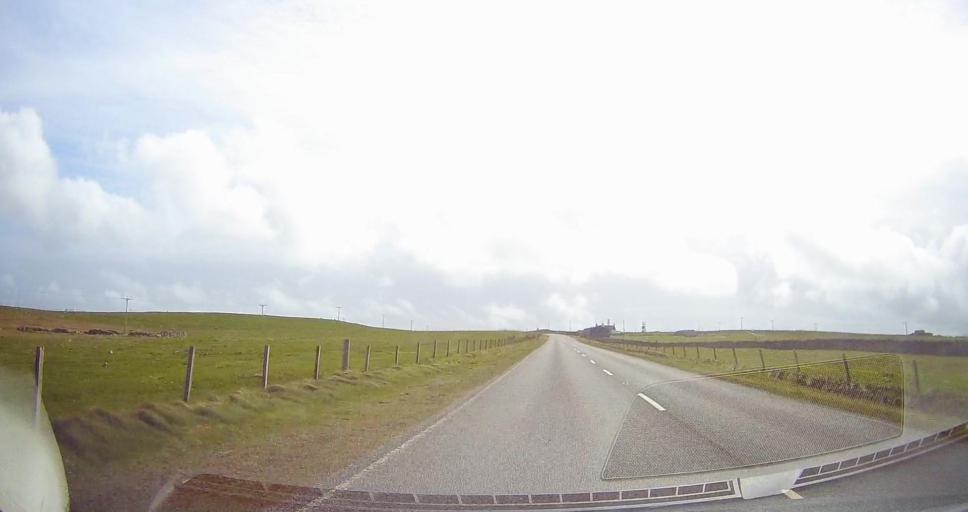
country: GB
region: Scotland
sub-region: Shetland Islands
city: Sandwick
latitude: 59.9164
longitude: -1.3006
